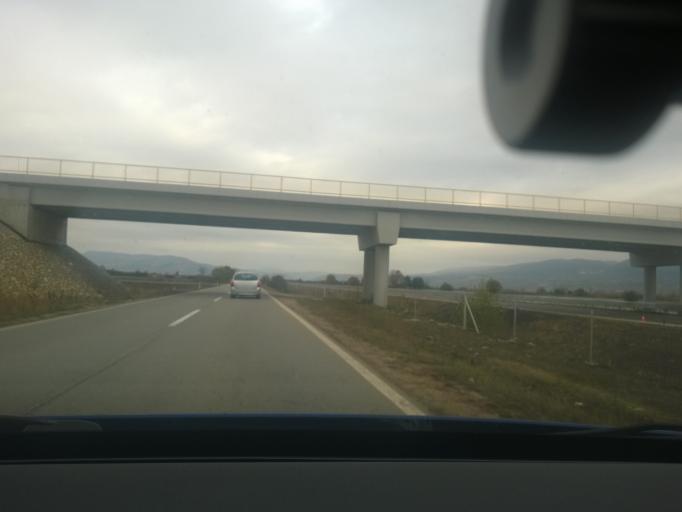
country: RS
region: Central Serbia
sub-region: Pirotski Okrug
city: Pirot
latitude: 43.0951
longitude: 22.6479
